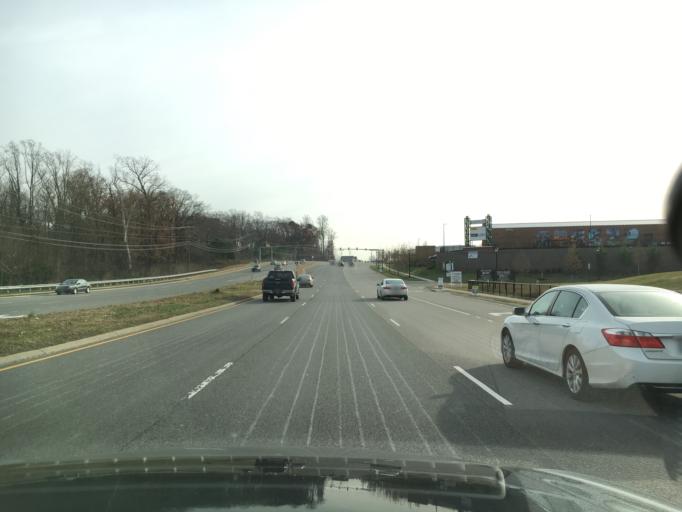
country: US
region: Virginia
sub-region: Henrico County
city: Short Pump
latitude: 37.6605
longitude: -77.6388
